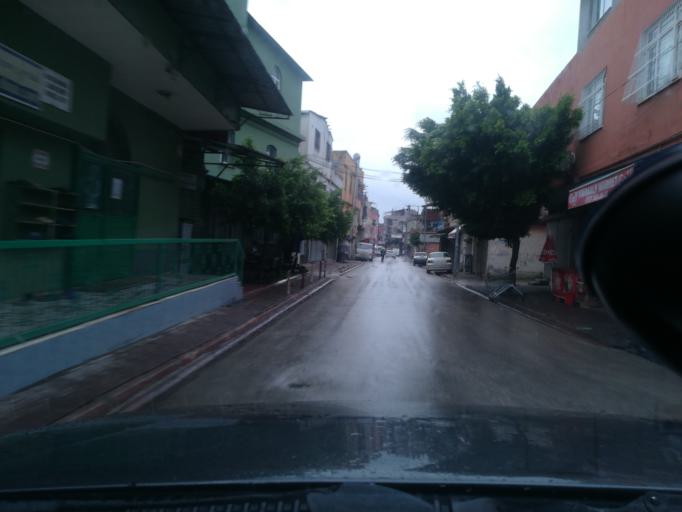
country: TR
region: Adana
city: Seyhan
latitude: 37.0191
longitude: 35.3008
